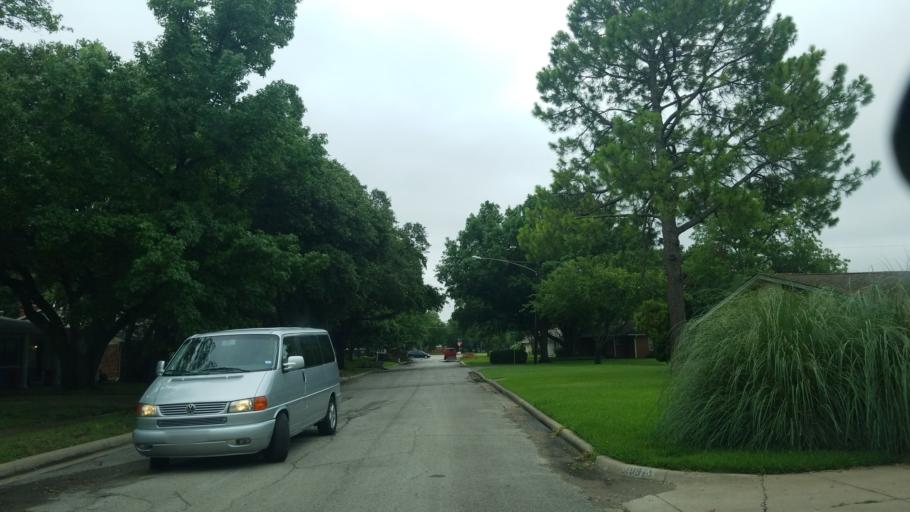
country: US
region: Texas
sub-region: Dallas County
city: Farmers Branch
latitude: 32.8967
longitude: -96.8646
